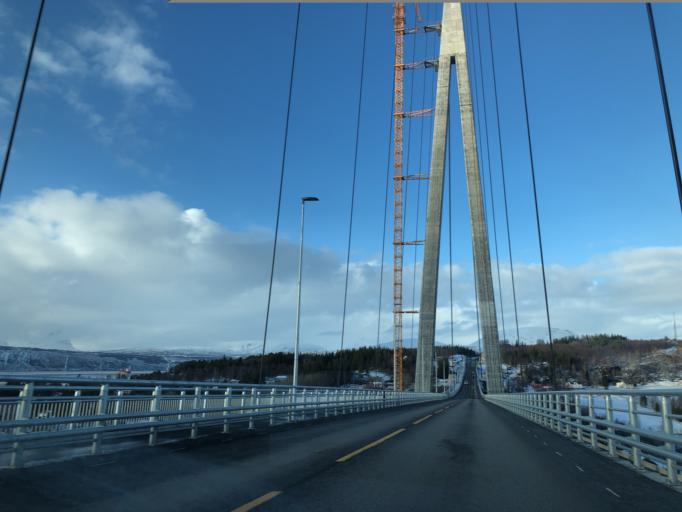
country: NO
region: Nordland
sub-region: Narvik
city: Narvik
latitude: 68.4632
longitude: 17.4817
